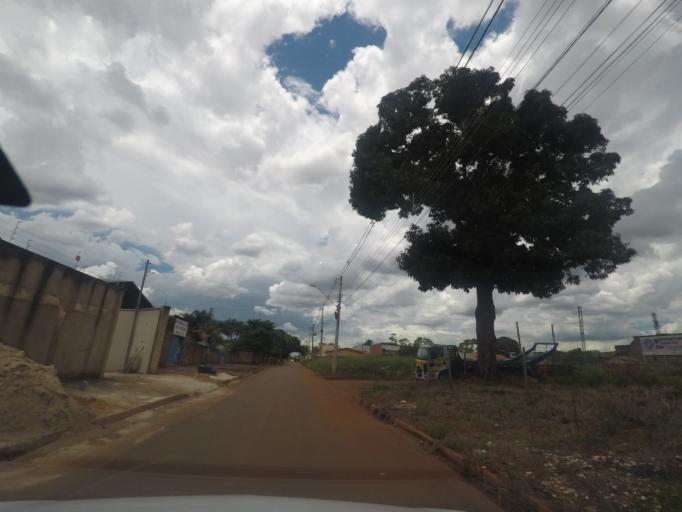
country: BR
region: Goias
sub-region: Goiania
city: Goiania
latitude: -16.7098
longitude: -49.3458
